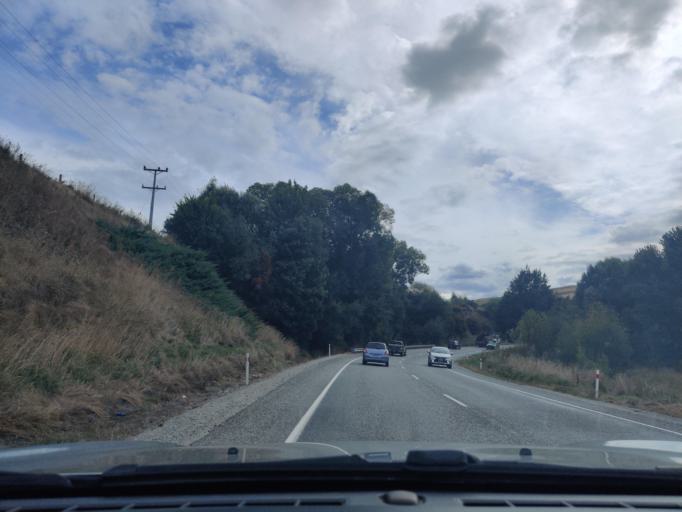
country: NZ
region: Otago
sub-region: Queenstown-Lakes District
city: Arrowtown
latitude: -44.9955
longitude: 168.8018
